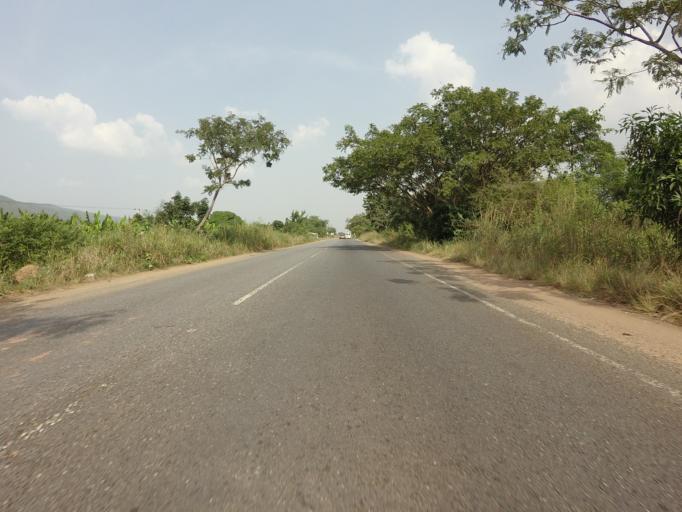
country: GH
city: Akropong
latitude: 5.9293
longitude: -0.0416
